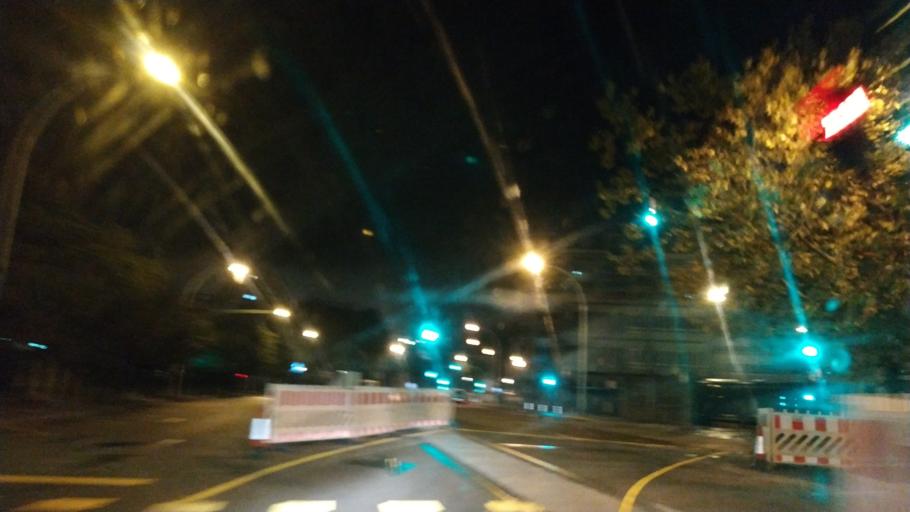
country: ES
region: Galicia
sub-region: Provincia da Coruna
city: A Coruna
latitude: 43.3541
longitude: -8.4037
